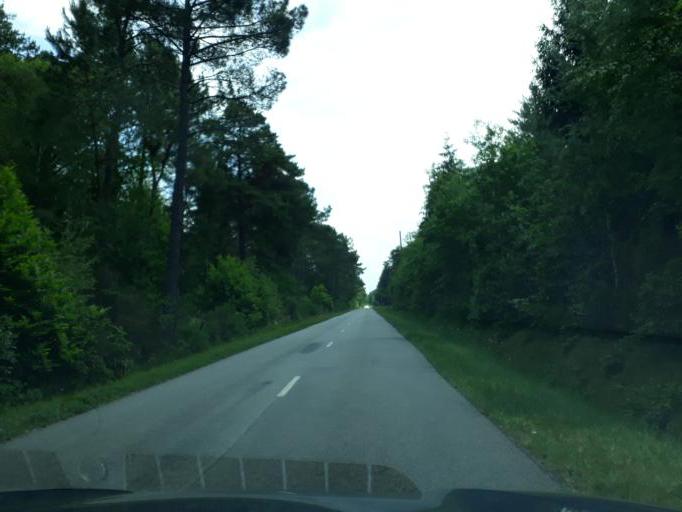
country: FR
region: Centre
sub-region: Departement du Loiret
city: Vienne-en-Val
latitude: 47.7496
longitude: 2.1410
